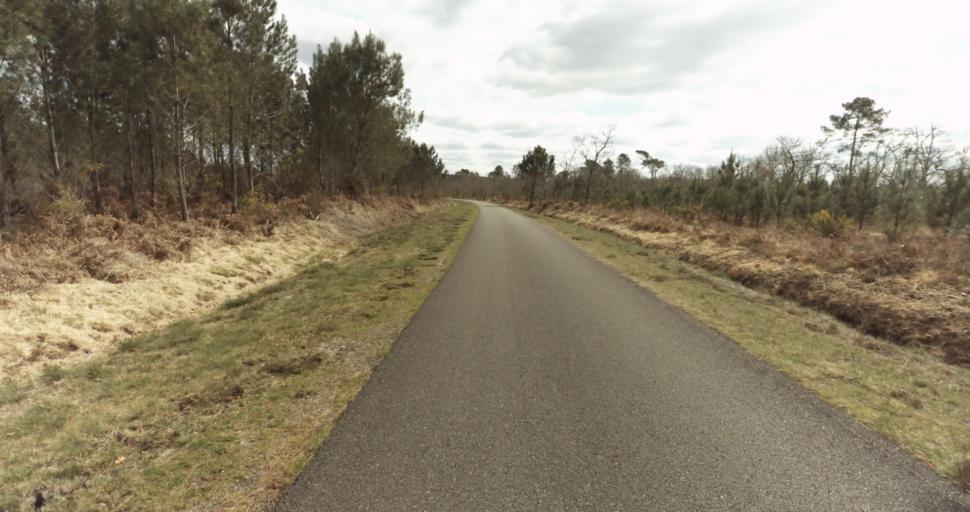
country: FR
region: Aquitaine
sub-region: Departement des Landes
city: Roquefort
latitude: 44.1062
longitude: -0.4475
